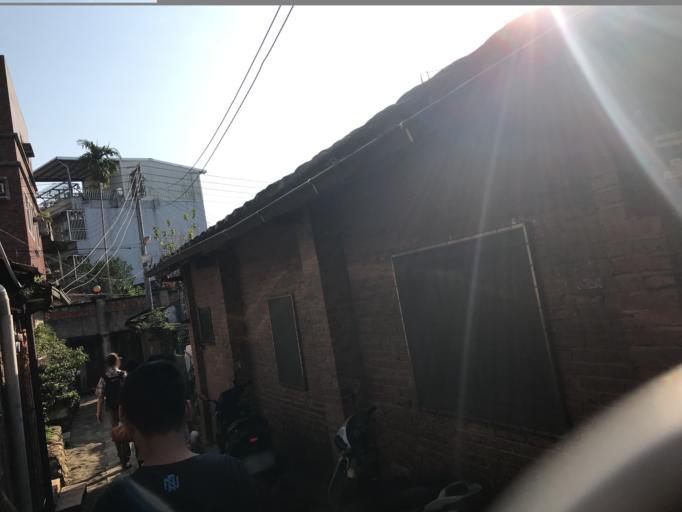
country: TW
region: Taiwan
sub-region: Hsinchu
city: Hsinchu
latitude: 24.6997
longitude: 121.0584
